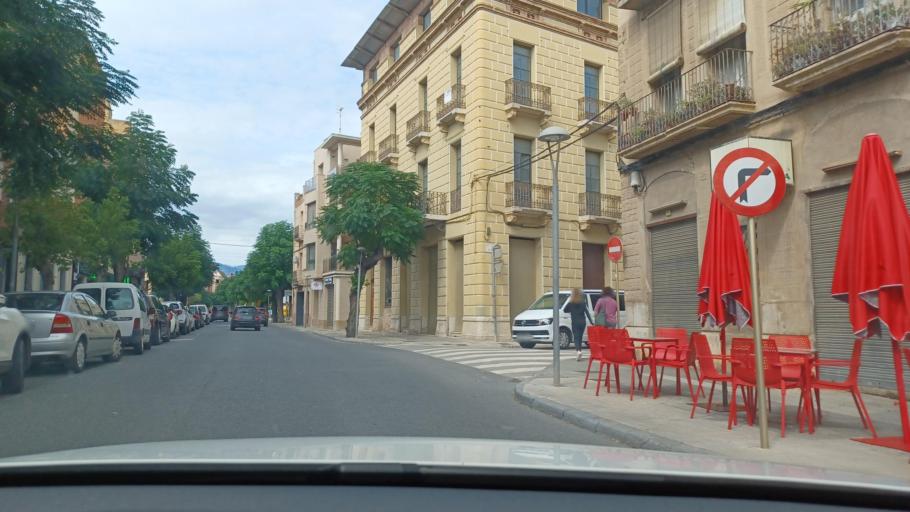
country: ES
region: Catalonia
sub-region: Provincia de Tarragona
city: Tortosa
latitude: 40.8152
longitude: 0.5173
